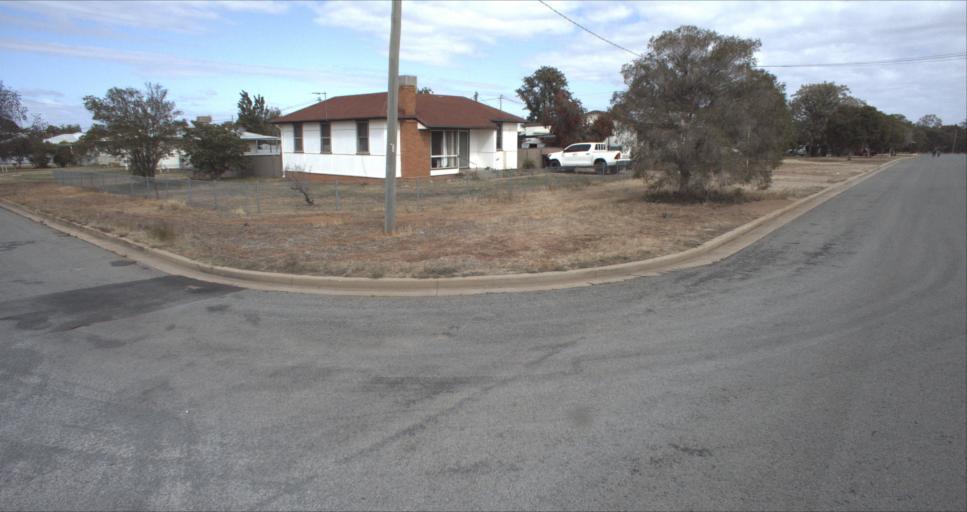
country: AU
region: New South Wales
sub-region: Leeton
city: Leeton
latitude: -34.5649
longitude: 146.3955
